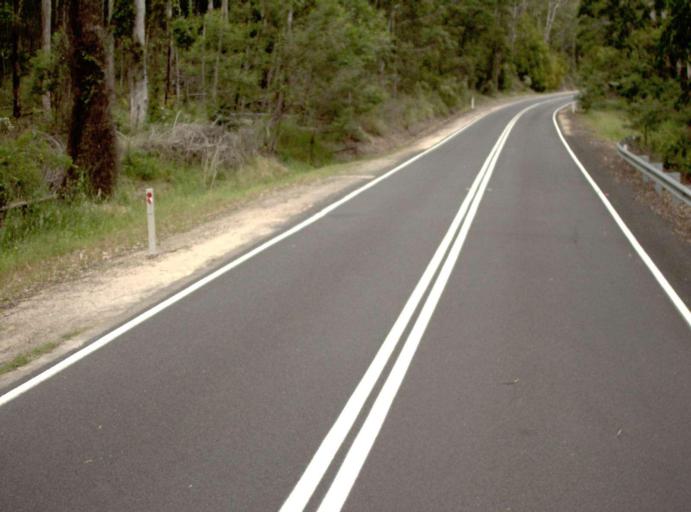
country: AU
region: New South Wales
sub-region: Bombala
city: Bombala
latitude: -37.4652
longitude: 149.1848
